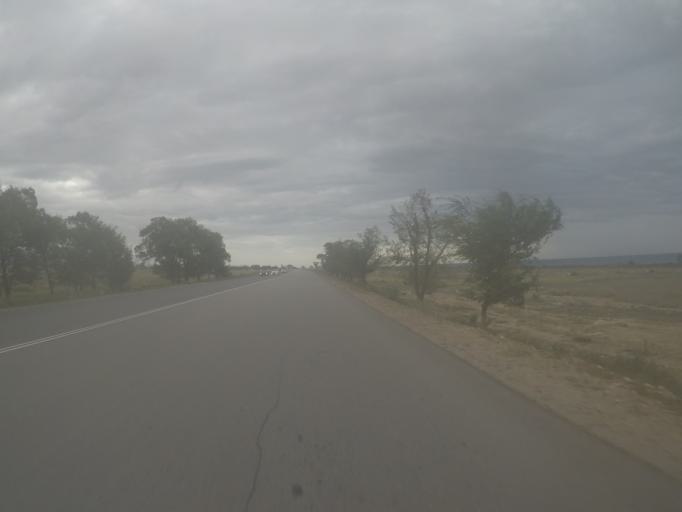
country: KG
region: Ysyk-Koel
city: Cholpon-Ata
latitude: 42.5970
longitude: 76.8393
